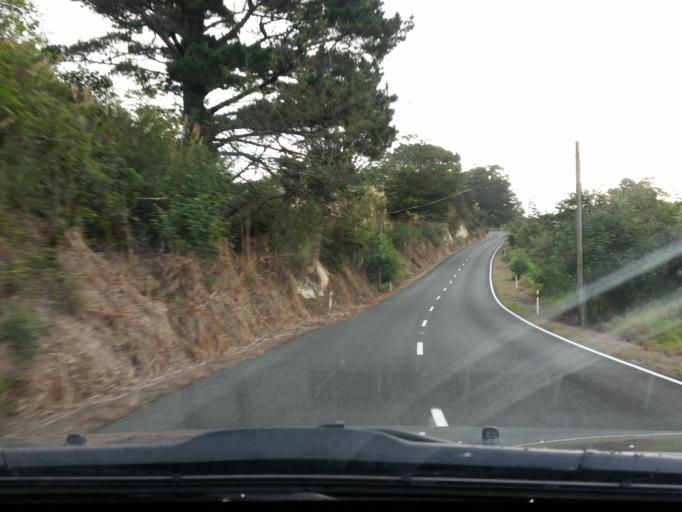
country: NZ
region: Northland
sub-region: Kaipara District
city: Dargaville
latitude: -35.8228
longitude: 173.6959
